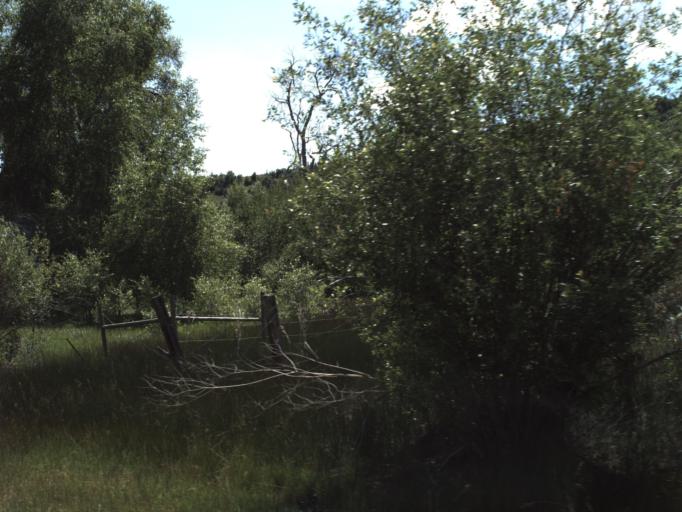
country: US
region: Utah
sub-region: Weber County
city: Wolf Creek
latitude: 41.3223
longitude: -111.6161
